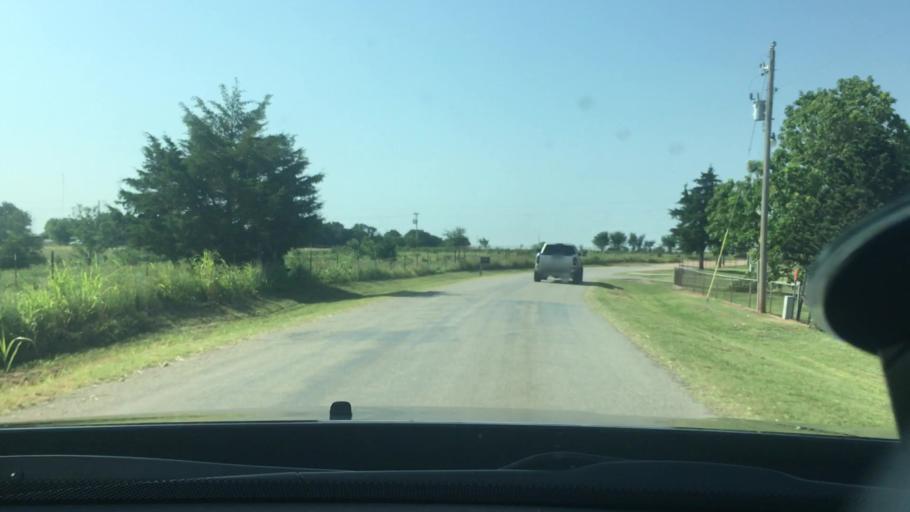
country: US
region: Oklahoma
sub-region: Garvin County
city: Lindsay
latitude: 34.7795
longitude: -97.6094
